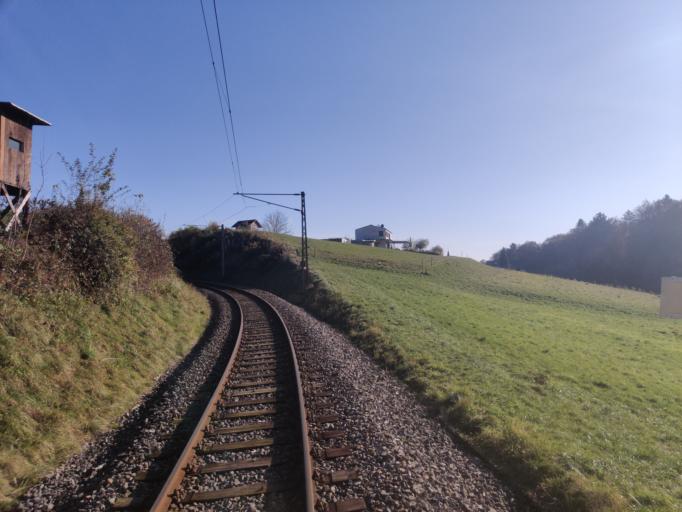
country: AT
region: Styria
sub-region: Politischer Bezirk Suedoststeiermark
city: Maierdorf
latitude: 46.8934
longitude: 15.8705
